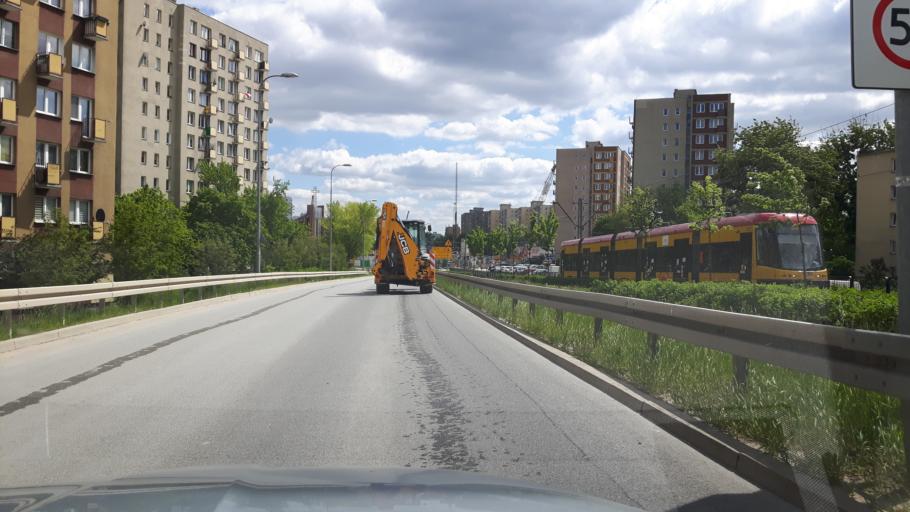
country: PL
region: Masovian Voivodeship
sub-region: Warszawa
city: Targowek
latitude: 52.2963
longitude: 21.0252
